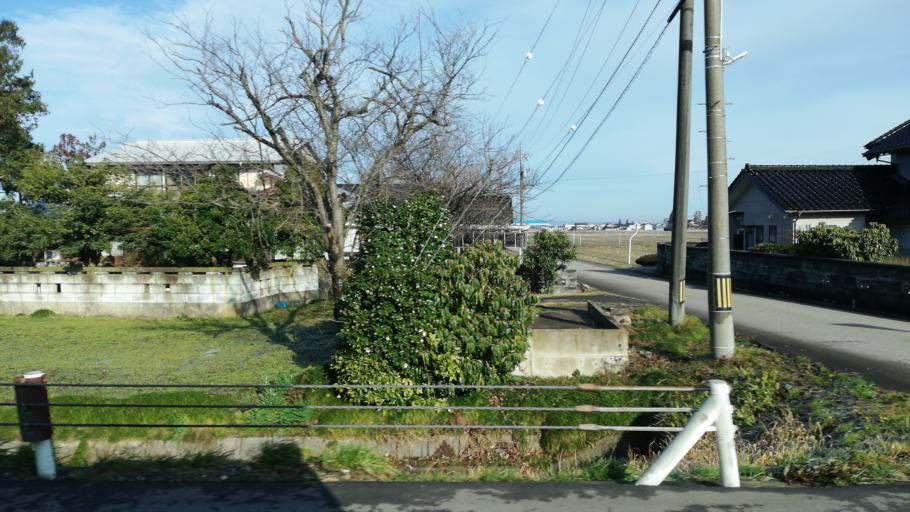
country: JP
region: Toyama
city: Nanto-shi
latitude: 36.5750
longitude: 136.9223
